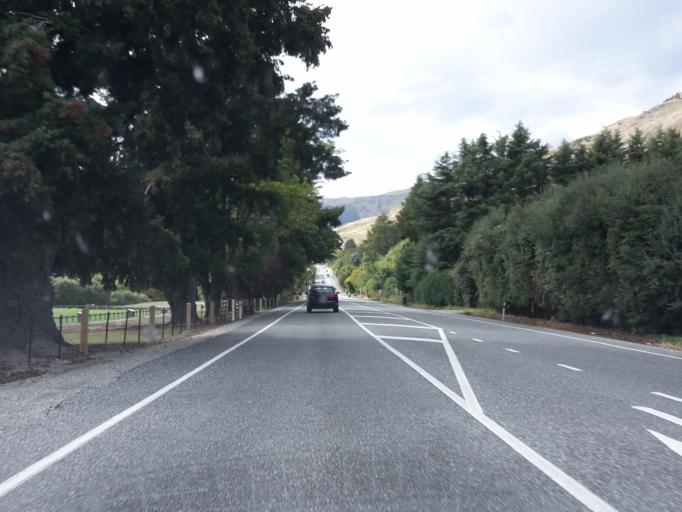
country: NZ
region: Otago
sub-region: Queenstown-Lakes District
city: Arrowtown
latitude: -44.9903
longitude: 168.8099
